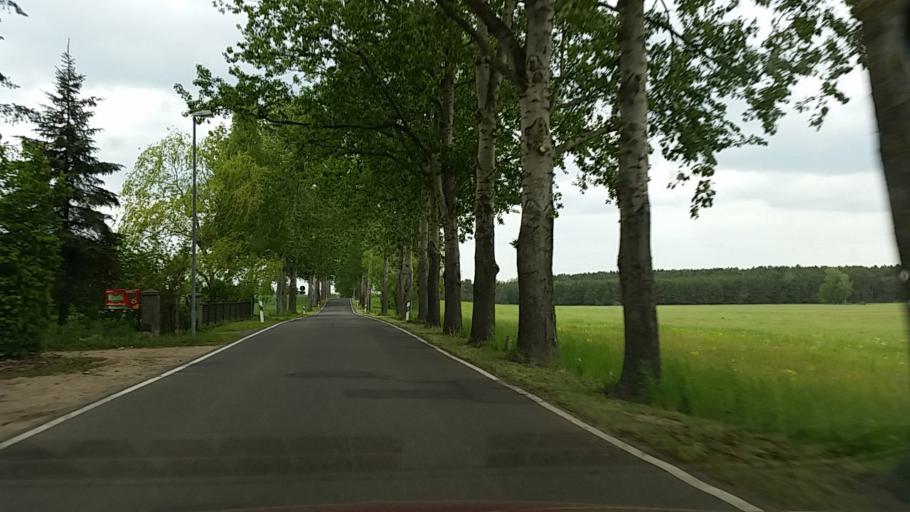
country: DE
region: Brandenburg
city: Rauen
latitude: 52.3180
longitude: 13.9621
